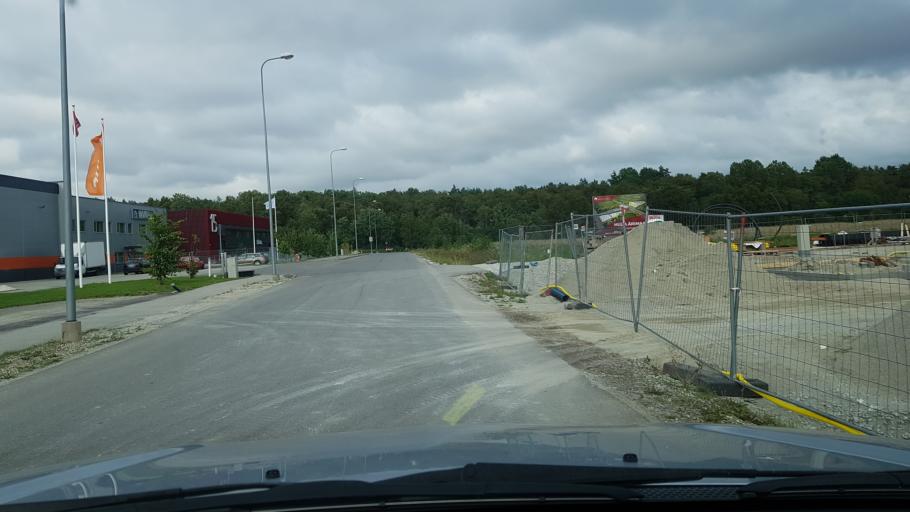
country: EE
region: Harju
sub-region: Tallinna linn
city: Kose
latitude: 59.3982
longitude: 24.8273
